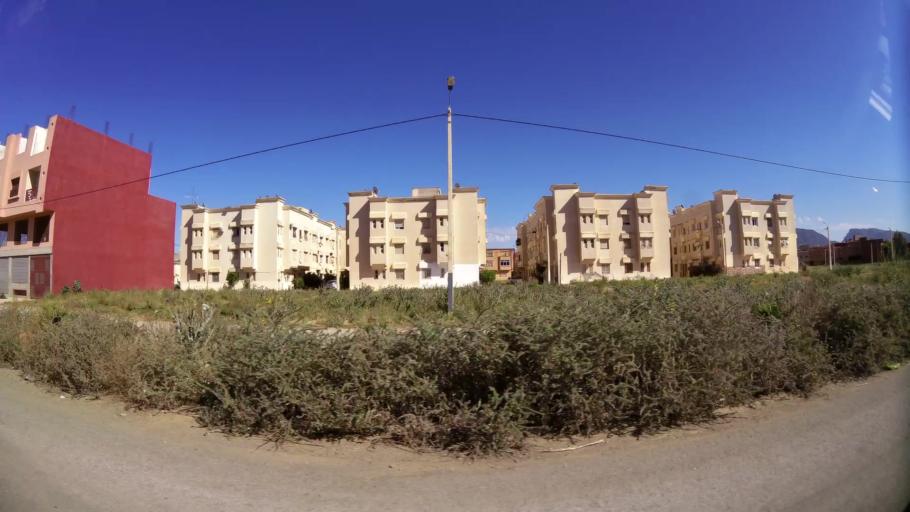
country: MA
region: Oriental
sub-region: Berkane-Taourirt
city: Berkane
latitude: 34.9420
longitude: -2.3373
